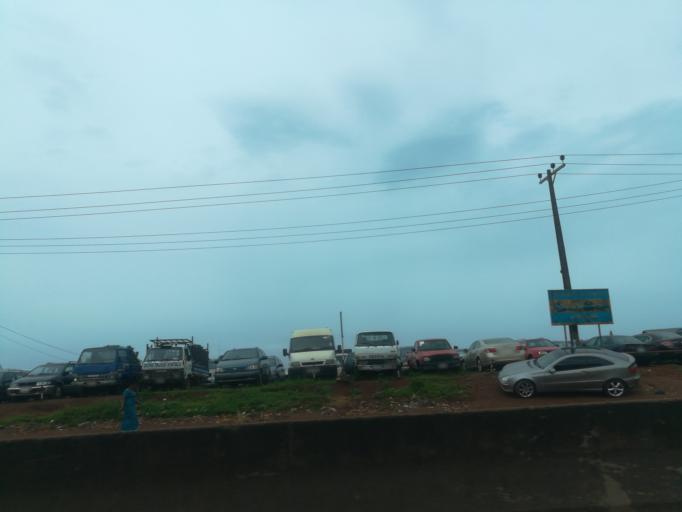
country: NG
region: Oyo
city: Ibadan
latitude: 7.3945
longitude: 3.9634
